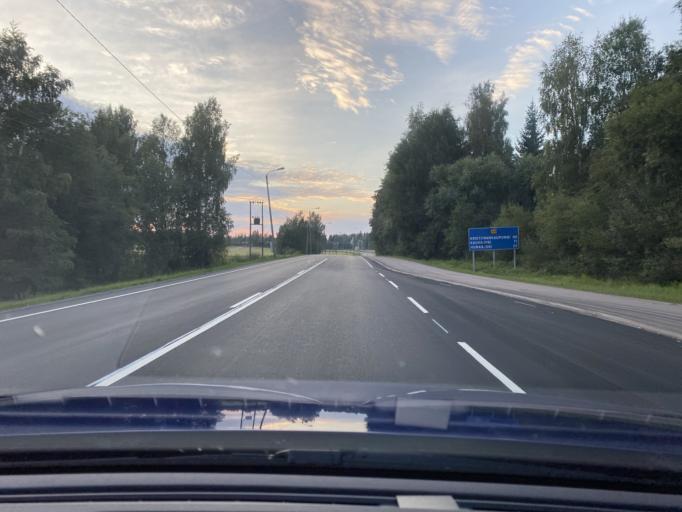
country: FI
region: Satakunta
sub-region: Pohjois-Satakunta
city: Kankaanpaeae
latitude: 61.8231
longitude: 22.3630
